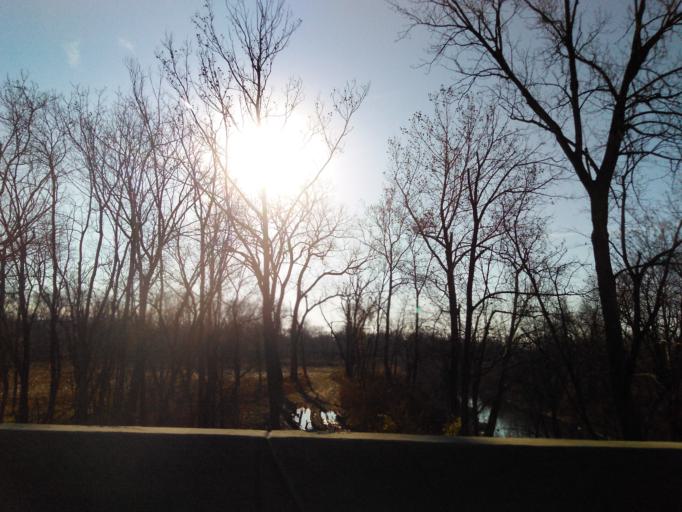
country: US
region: Illinois
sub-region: Bond County
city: Greenville
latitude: 38.8369
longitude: -89.5038
